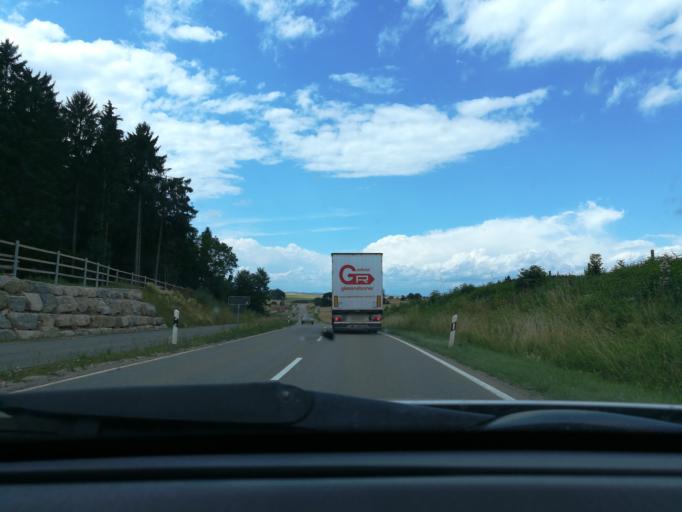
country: DE
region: Baden-Wuerttemberg
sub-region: Freiburg Region
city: Bosingen
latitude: 48.2010
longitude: 8.5486
